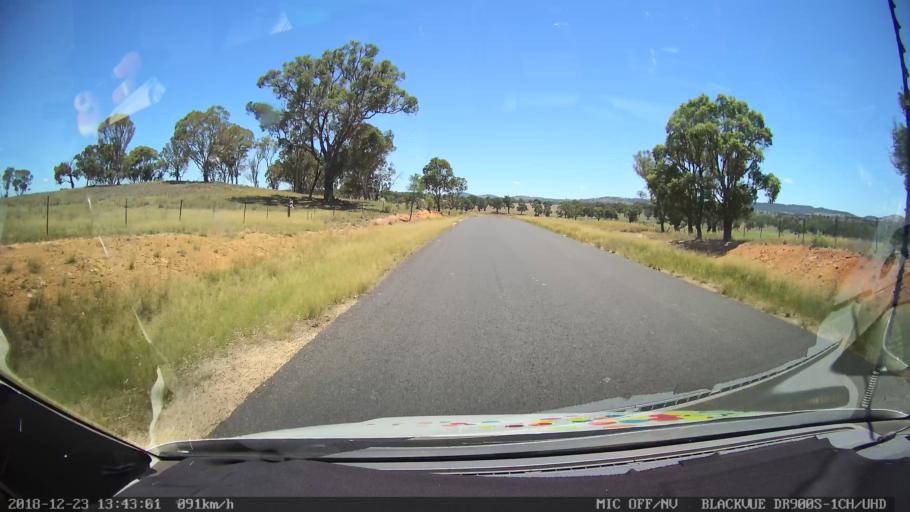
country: AU
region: New South Wales
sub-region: Tamworth Municipality
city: Manilla
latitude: -30.4828
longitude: 151.1559
